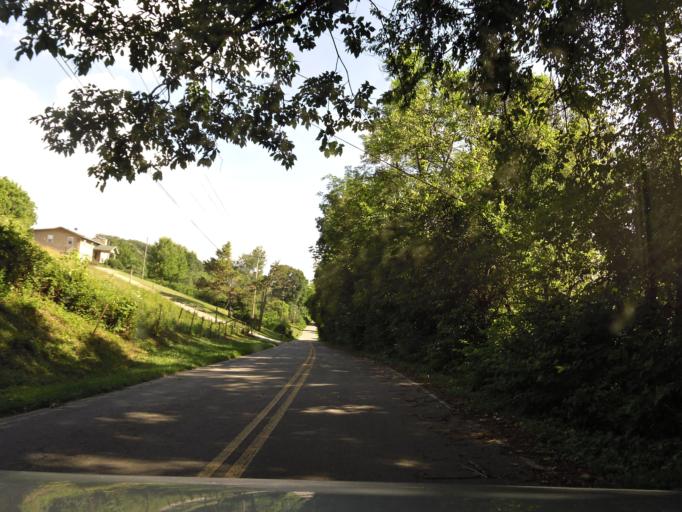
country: US
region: Tennessee
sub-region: Union County
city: Condon
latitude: 36.1289
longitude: -83.9134
